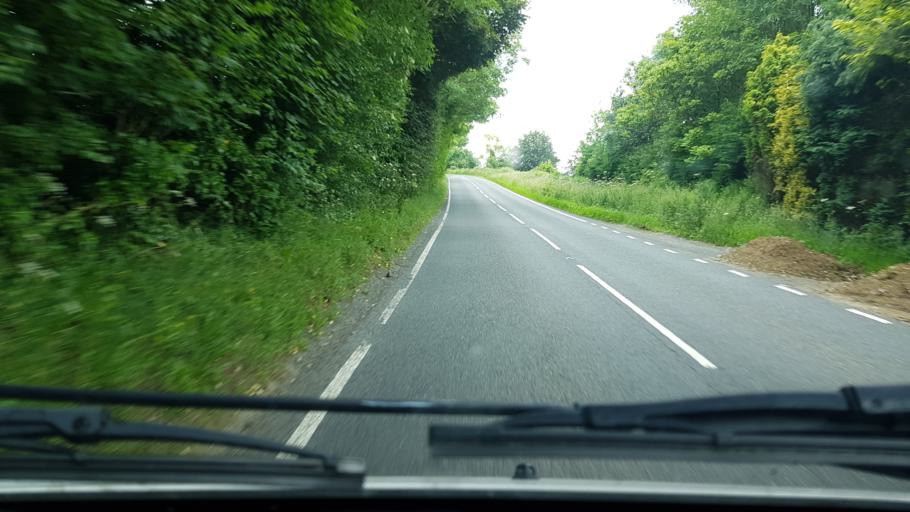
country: GB
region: England
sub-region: Gloucestershire
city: Stow on the Wold
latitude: 51.9384
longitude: -1.7282
